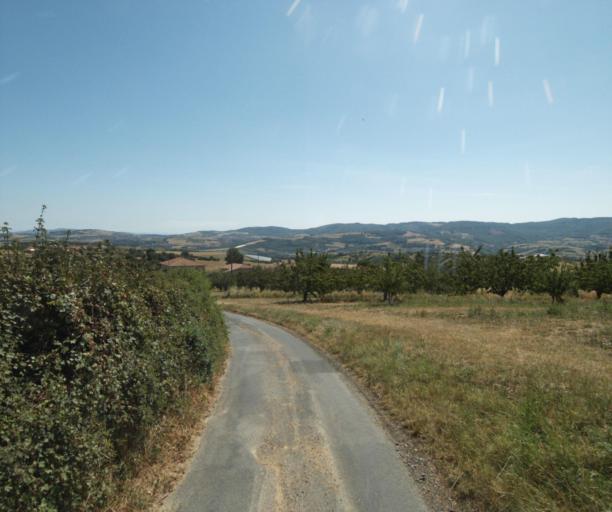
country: FR
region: Rhone-Alpes
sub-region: Departement du Rhone
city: Bessenay
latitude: 45.7930
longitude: 4.5439
